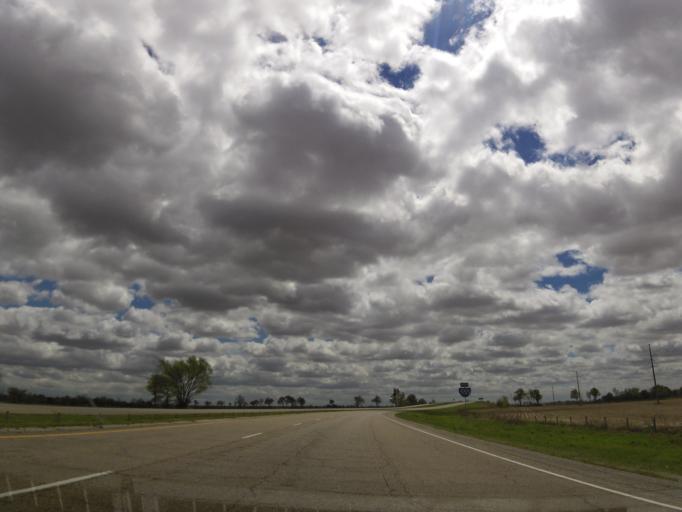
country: US
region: Arkansas
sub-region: Poinsett County
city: Trumann
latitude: 35.6258
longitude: -90.4966
